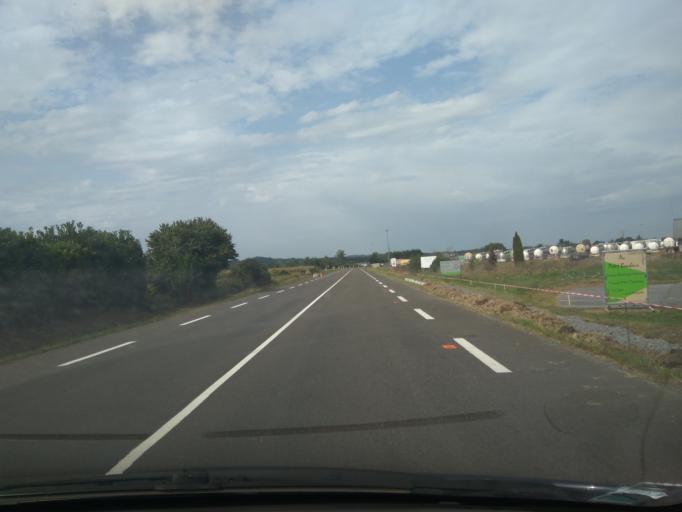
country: FR
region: Aquitaine
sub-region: Departement des Pyrenees-Atlantiques
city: Monein
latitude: 43.3620
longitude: -0.5681
